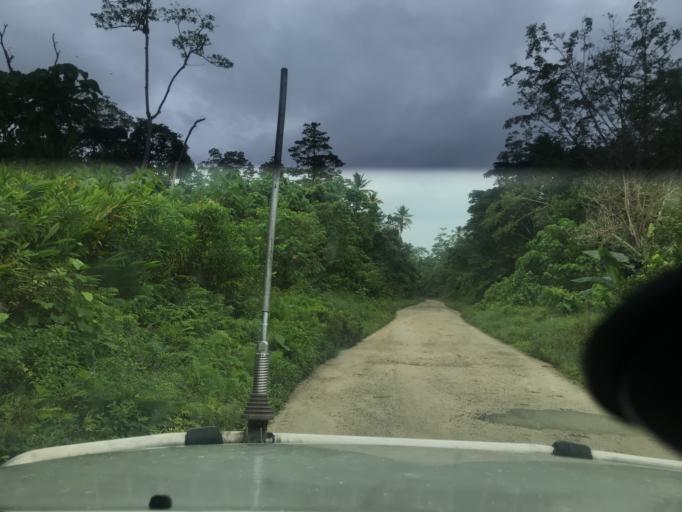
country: SB
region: Choiseul
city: Taro'a
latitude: -9.1386
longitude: 160.8533
